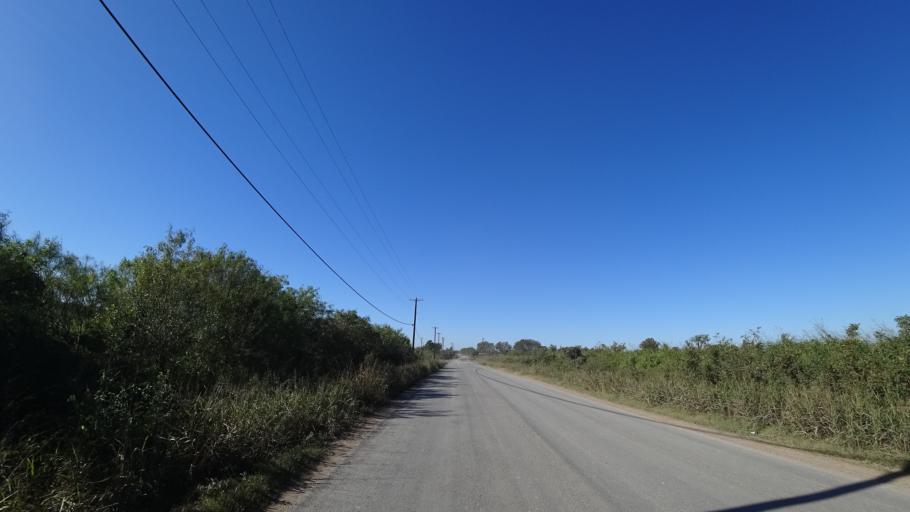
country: US
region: Texas
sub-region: Travis County
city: Hornsby Bend
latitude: 30.2407
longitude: -97.6552
